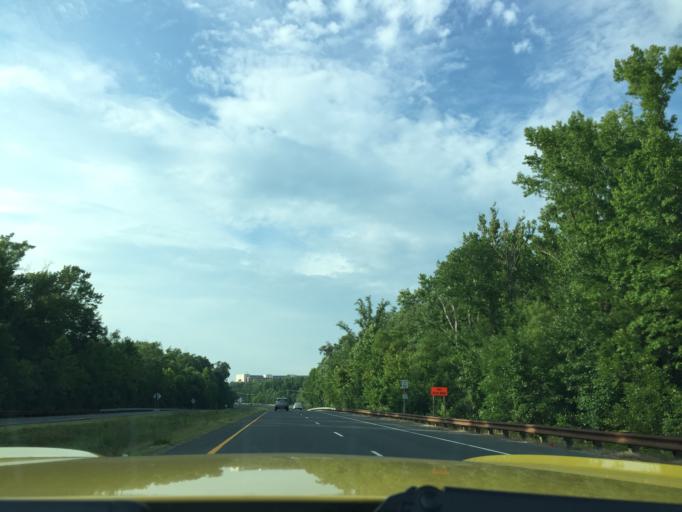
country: US
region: Virginia
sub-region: Fairfax County
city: Fort Belvoir
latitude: 38.7109
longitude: -77.1639
